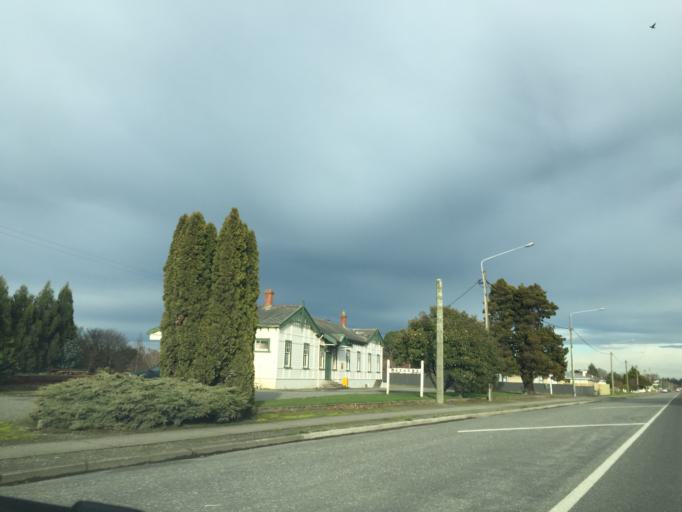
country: NZ
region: Southland
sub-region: Gore District
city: Gore
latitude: -46.1952
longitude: 168.8636
